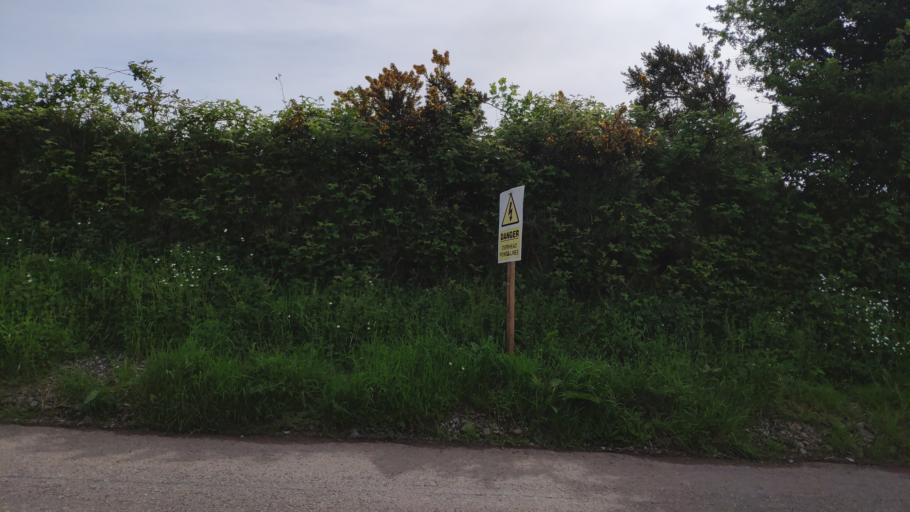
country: IE
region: Munster
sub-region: County Cork
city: Blarney
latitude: 51.9764
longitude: -8.5135
